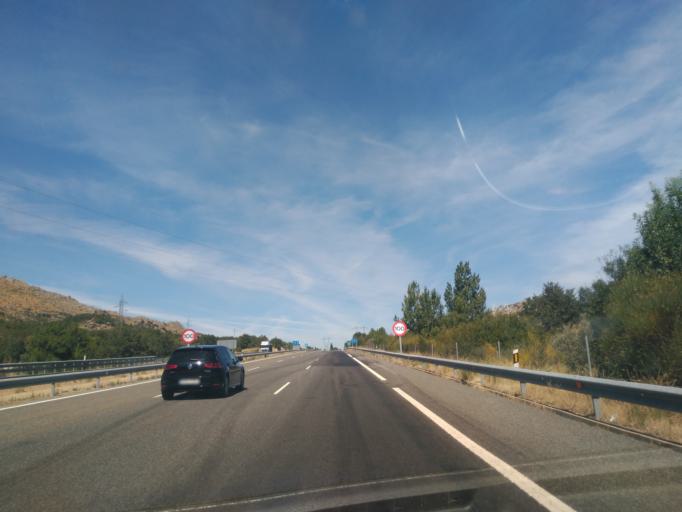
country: ES
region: Castille and Leon
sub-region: Provincia de Salamanca
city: Vallejera de Riofrio
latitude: 40.4053
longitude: -5.7290
